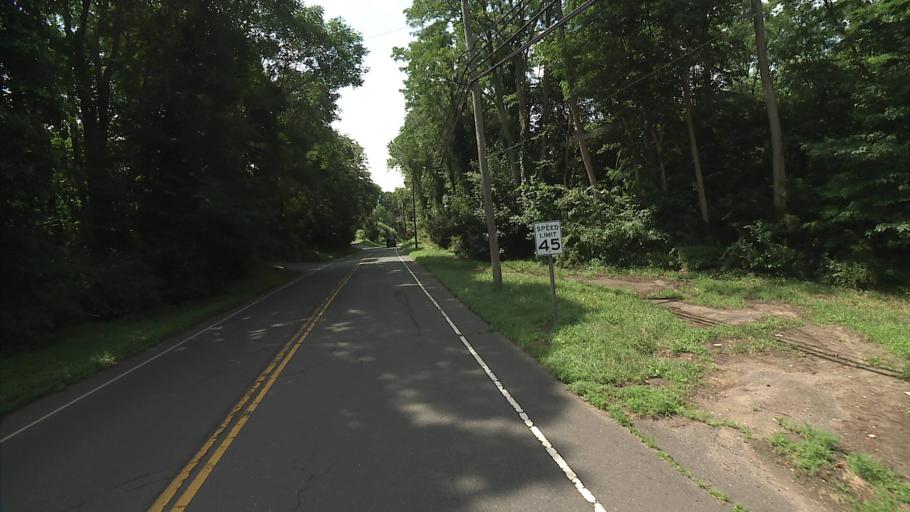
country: US
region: Connecticut
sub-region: Middlesex County
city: Cromwell
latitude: 41.6147
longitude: -72.5990
